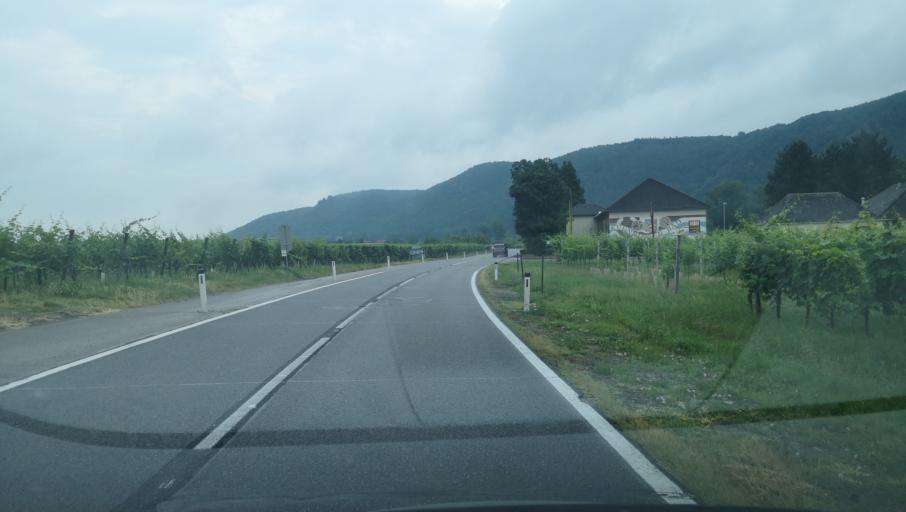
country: AT
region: Lower Austria
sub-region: Politischer Bezirk Krems
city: Durnstein
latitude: 48.3892
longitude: 15.5246
